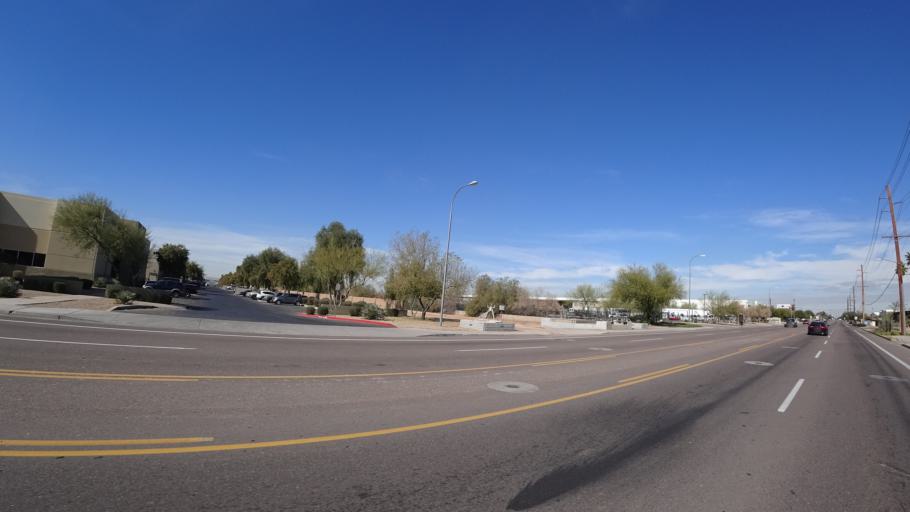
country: US
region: Arizona
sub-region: Maricopa County
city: Tolleson
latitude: 33.4406
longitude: -112.2036
